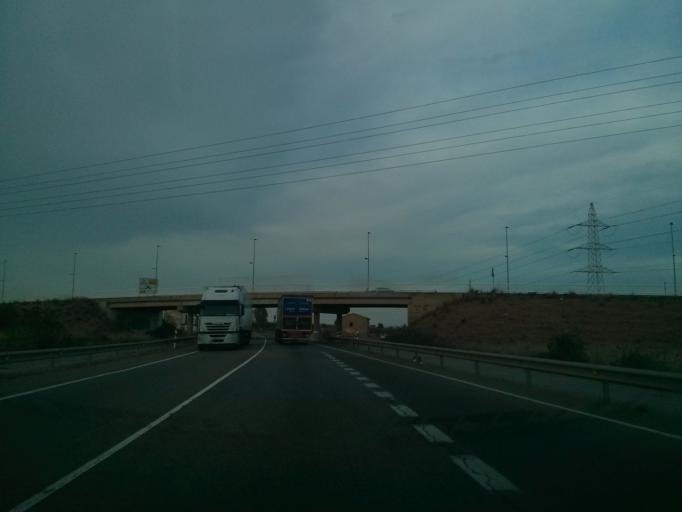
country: ES
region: Valencia
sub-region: Provincia de Castello
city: Vila-real
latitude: 39.9273
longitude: -0.0971
